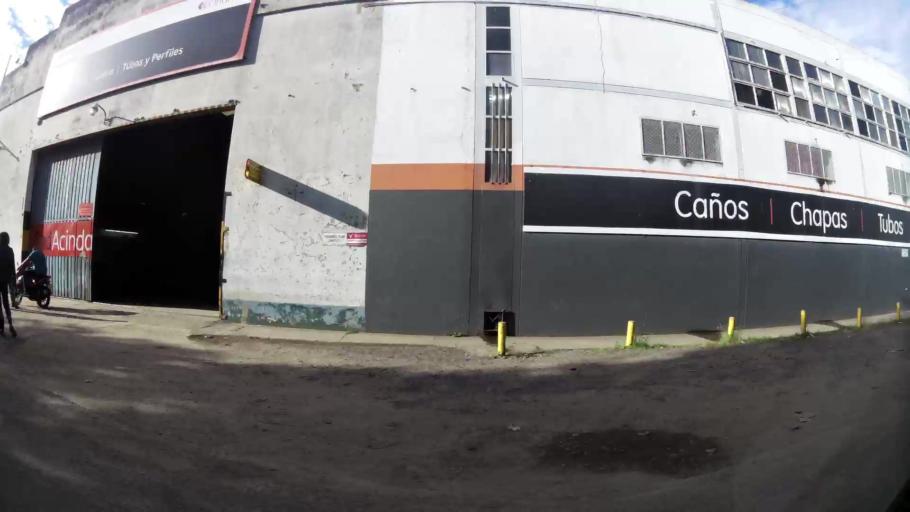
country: AR
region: Santa Fe
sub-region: Departamento de Rosario
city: Rosario
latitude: -32.9795
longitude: -60.6709
